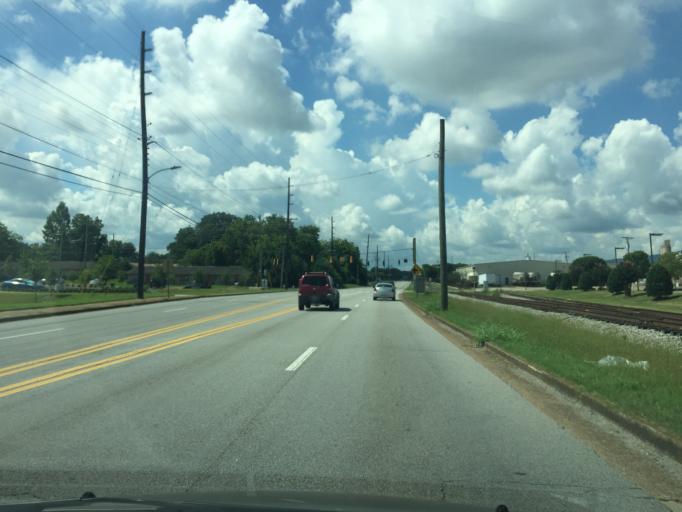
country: US
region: Tennessee
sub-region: Hamilton County
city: East Chattanooga
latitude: 35.0496
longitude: -85.2769
